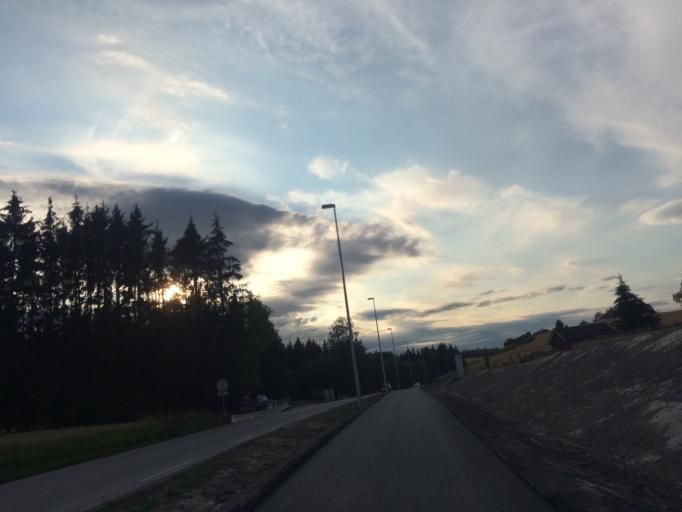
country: NO
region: Akershus
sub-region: Ski
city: Ski
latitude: 59.6839
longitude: 10.8743
